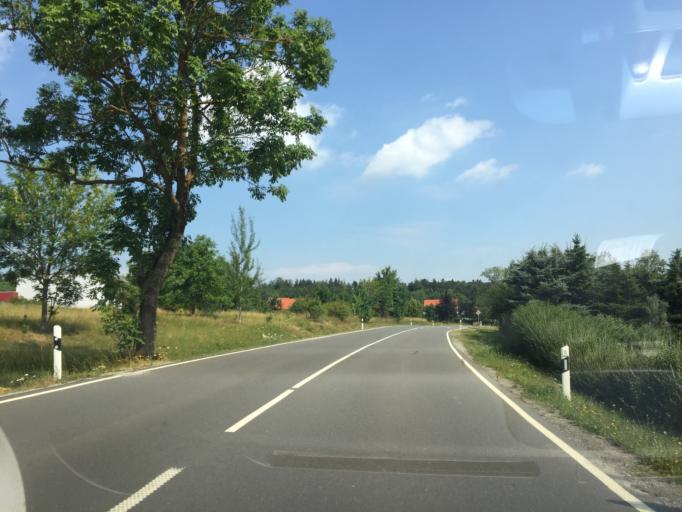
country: DE
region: Saxony-Anhalt
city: Elbingerode
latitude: 51.7667
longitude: 10.7853
